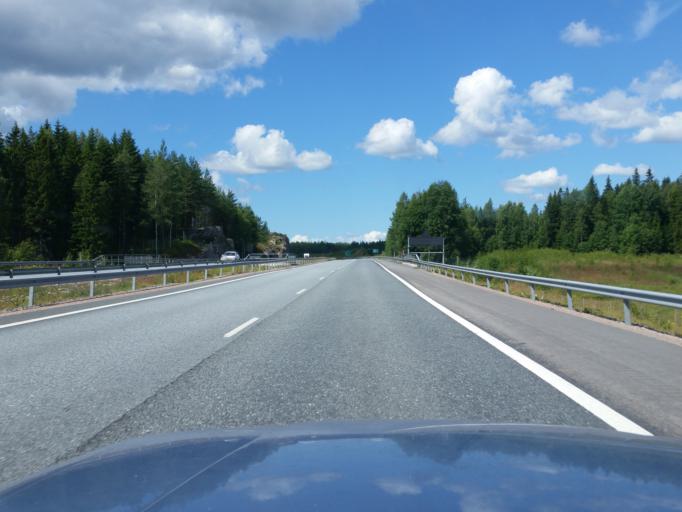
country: FI
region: Uusimaa
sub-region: Helsinki
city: Sammatti
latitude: 60.3800
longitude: 23.7893
